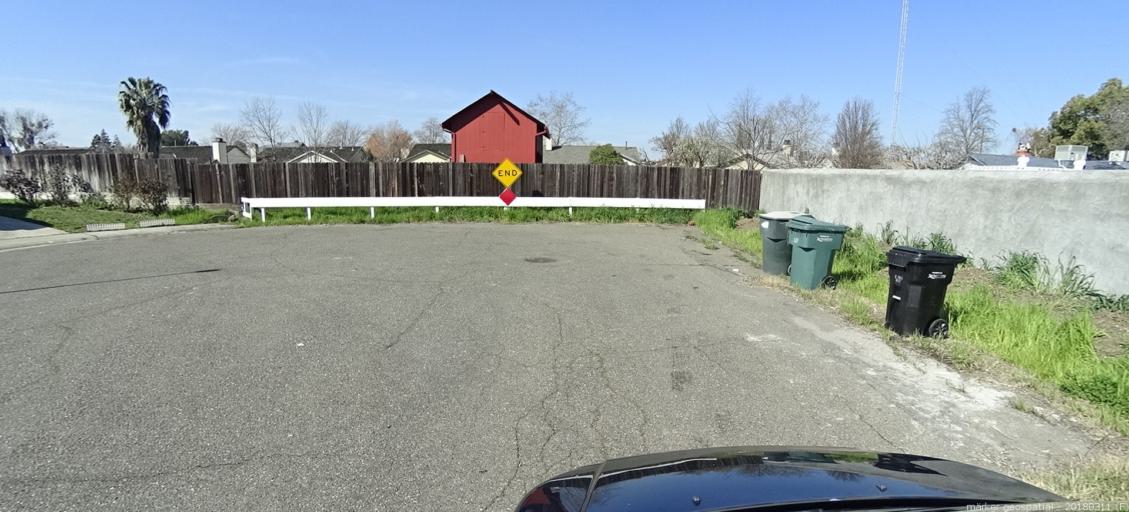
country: US
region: California
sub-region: Sacramento County
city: Florin
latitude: 38.4645
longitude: -121.4011
